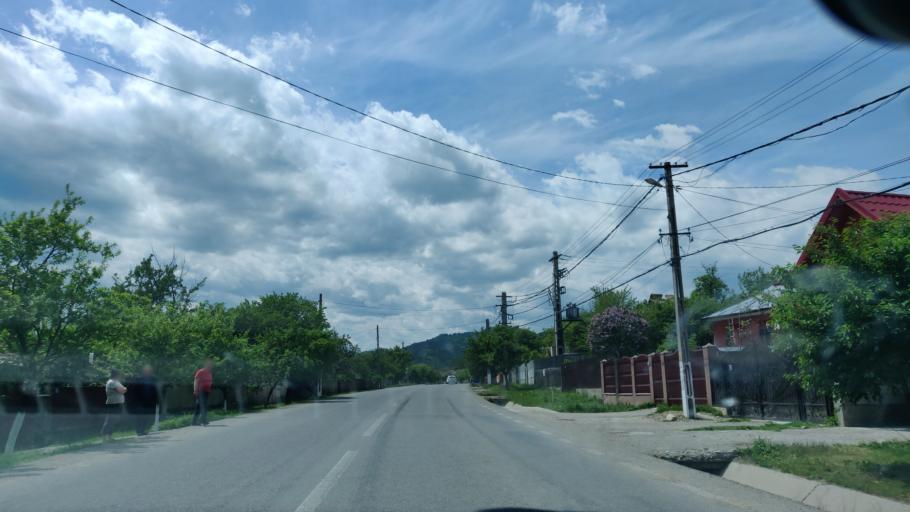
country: RO
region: Vrancea
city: Matacina
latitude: 45.8904
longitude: 26.8333
